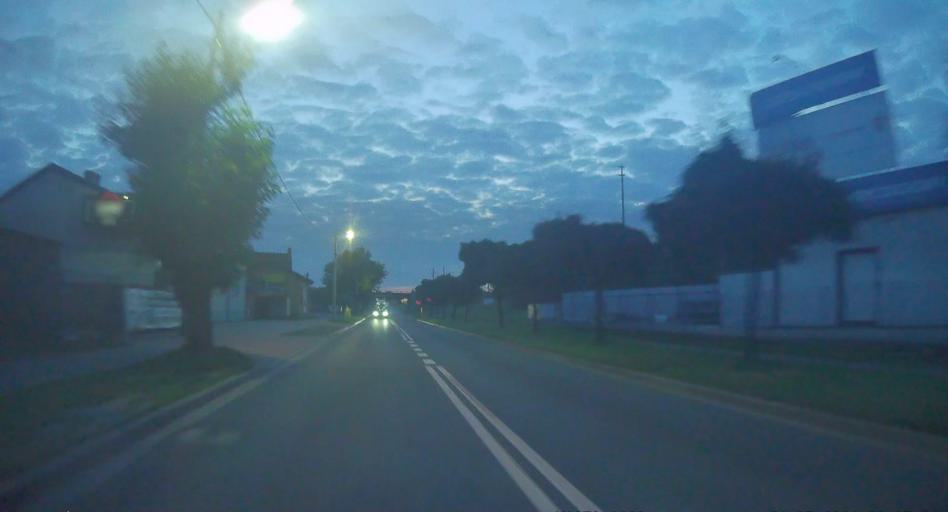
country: PL
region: Silesian Voivodeship
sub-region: Powiat klobucki
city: Klobuck
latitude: 50.9045
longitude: 18.9257
